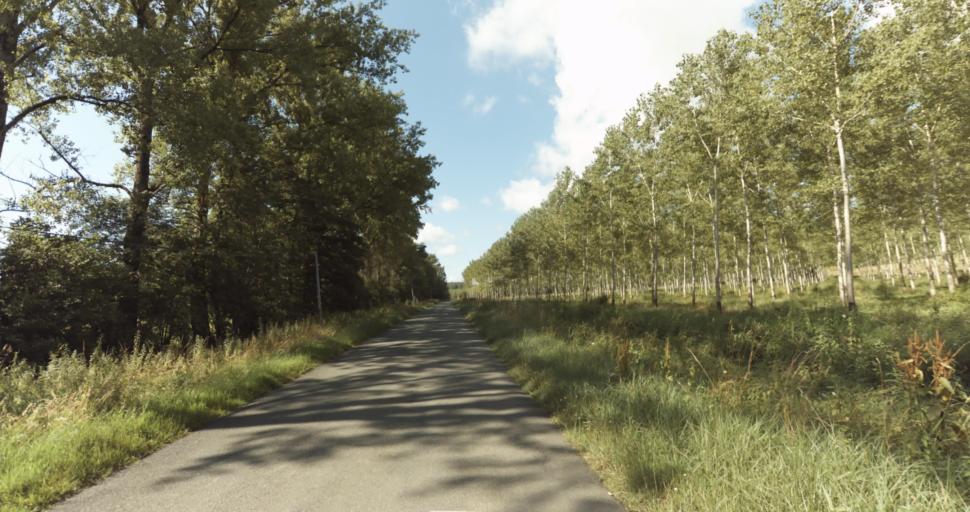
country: FR
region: Aquitaine
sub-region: Departement de la Gironde
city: Bazas
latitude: 44.4528
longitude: -0.1633
